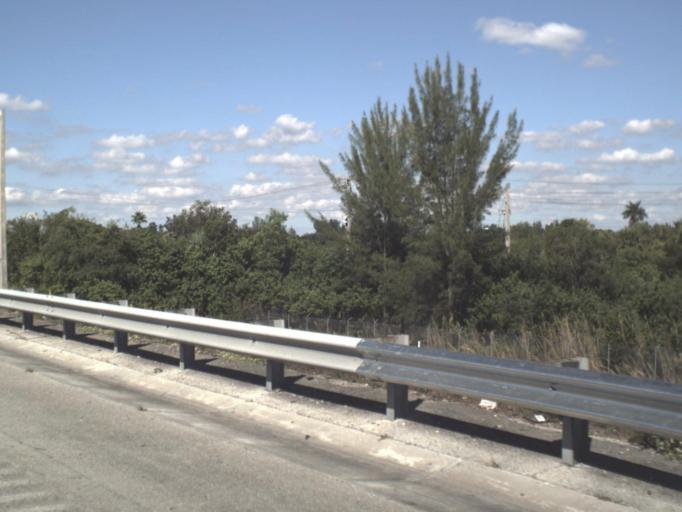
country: US
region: Florida
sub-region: Miami-Dade County
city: Country Club
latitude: 25.9709
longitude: -80.3099
